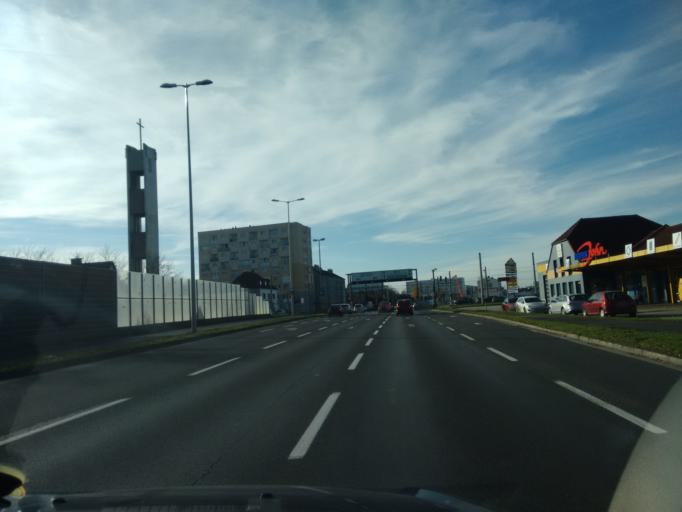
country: AT
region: Upper Austria
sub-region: Politischer Bezirk Linz-Land
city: Leonding
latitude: 48.2562
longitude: 14.2890
